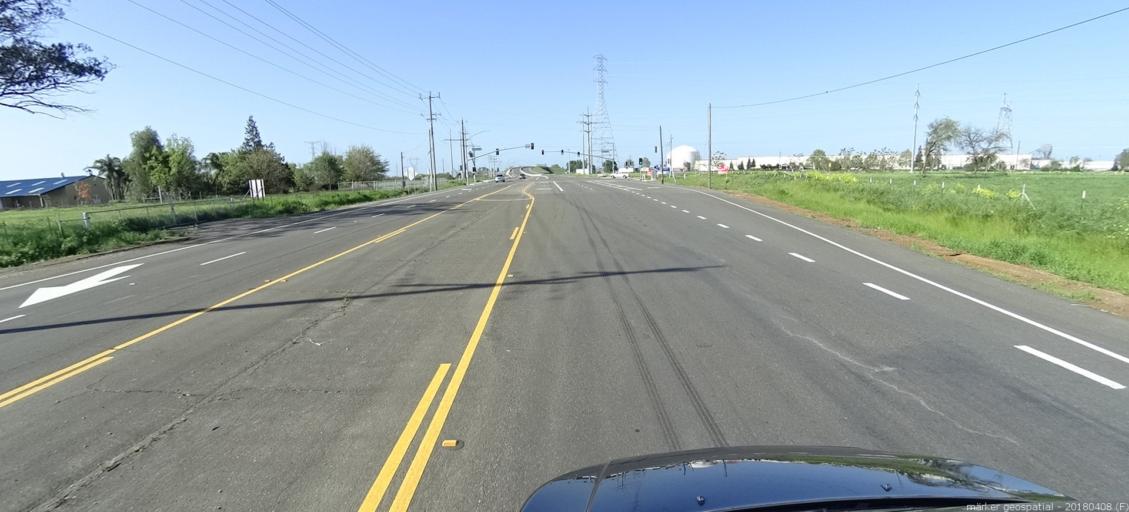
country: US
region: California
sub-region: Sacramento County
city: Elk Grove
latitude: 38.3863
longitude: -121.3489
